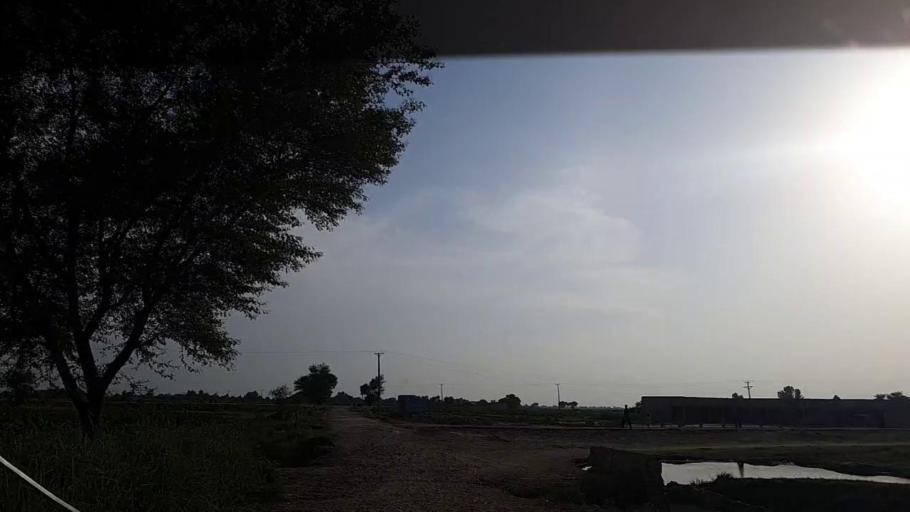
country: PK
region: Sindh
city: Khanpur
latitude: 27.8259
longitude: 69.3459
